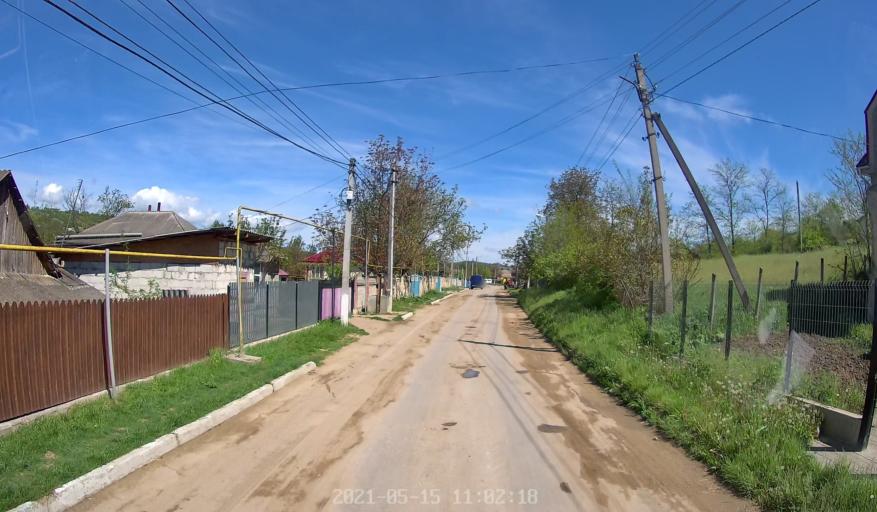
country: MD
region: Hincesti
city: Hincesti
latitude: 46.8289
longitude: 28.6765
